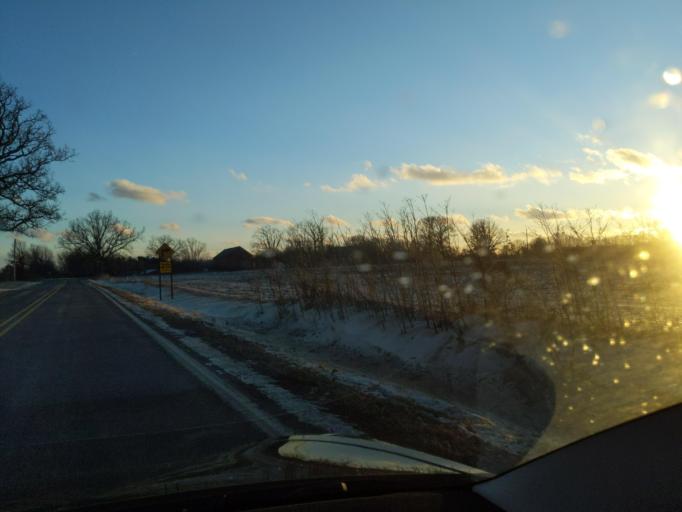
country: US
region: Michigan
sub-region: Ingham County
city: Stockbridge
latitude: 42.4486
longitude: -84.2097
